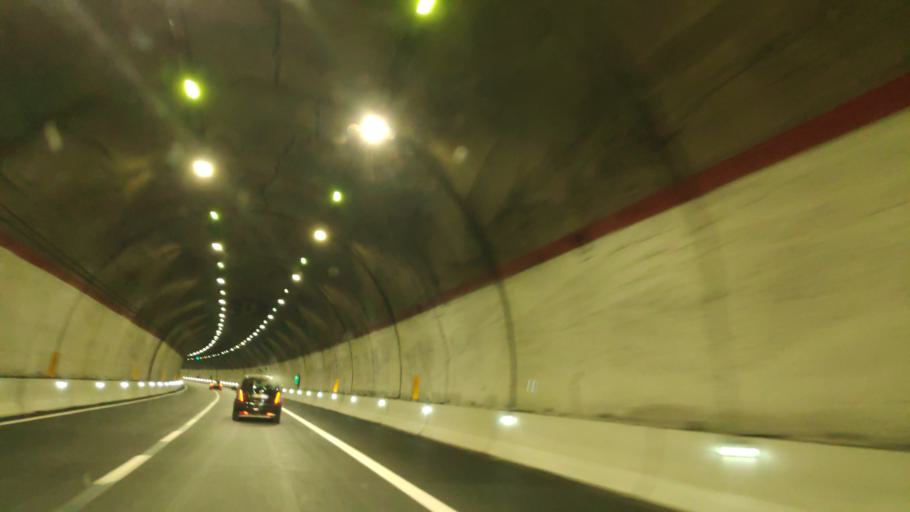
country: IT
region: Calabria
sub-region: Provincia di Reggio Calabria
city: Seminara
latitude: 38.3326
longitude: 15.8575
